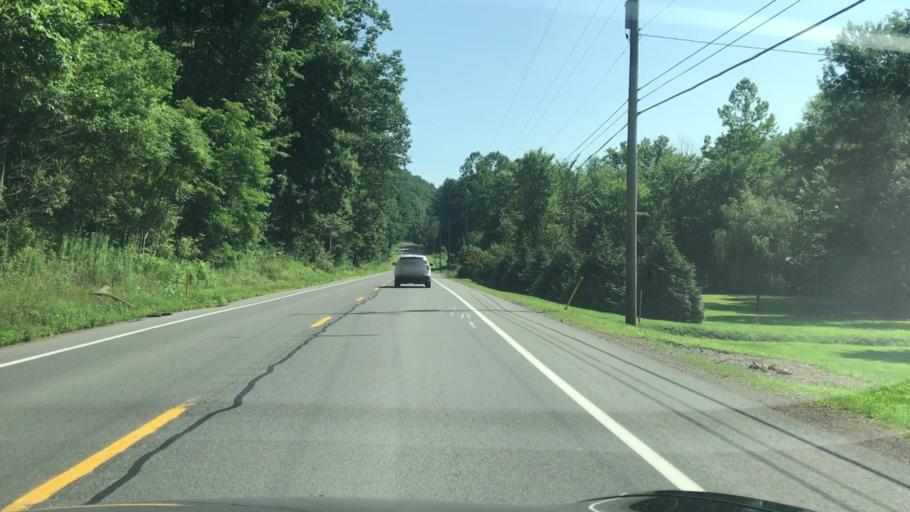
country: US
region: Pennsylvania
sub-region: Lycoming County
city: Garden View
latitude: 41.4333
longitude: -77.0036
